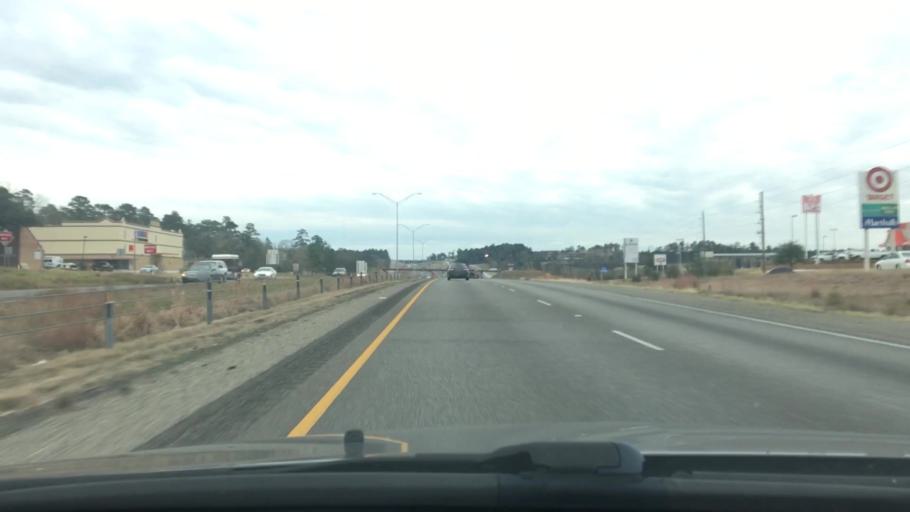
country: US
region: Texas
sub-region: Walker County
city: Huntsville
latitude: 30.7092
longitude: -95.5639
